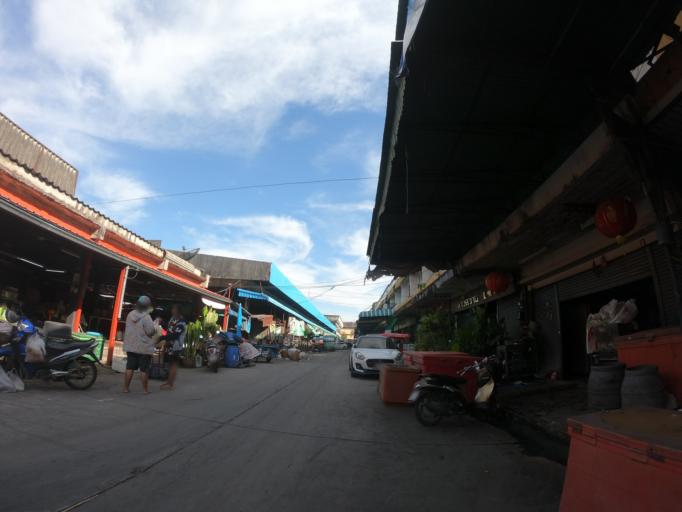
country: TH
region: Khon Kaen
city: Khon Kaen
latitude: 16.4376
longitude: 102.8323
